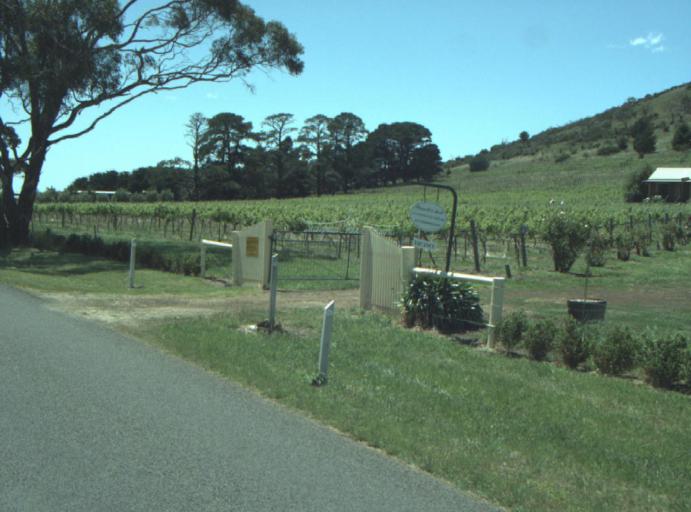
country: AU
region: Victoria
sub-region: Greater Geelong
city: Lara
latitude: -37.8837
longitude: 144.2595
